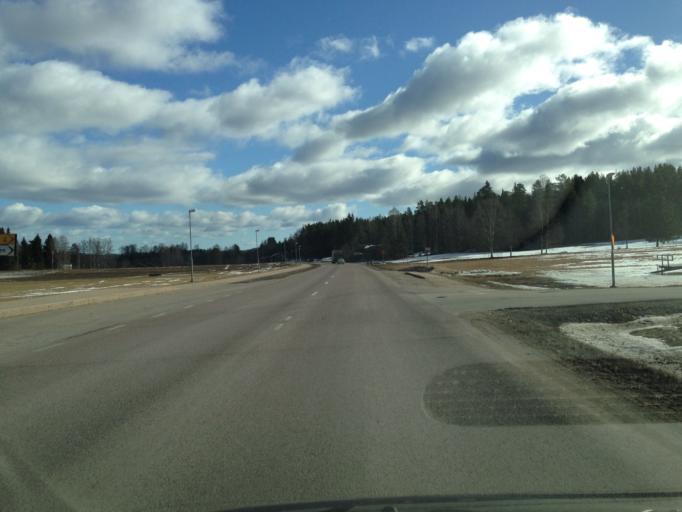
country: SE
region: Gaevleborg
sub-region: Ljusdals Kommun
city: Farila
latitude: 61.8008
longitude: 15.8584
